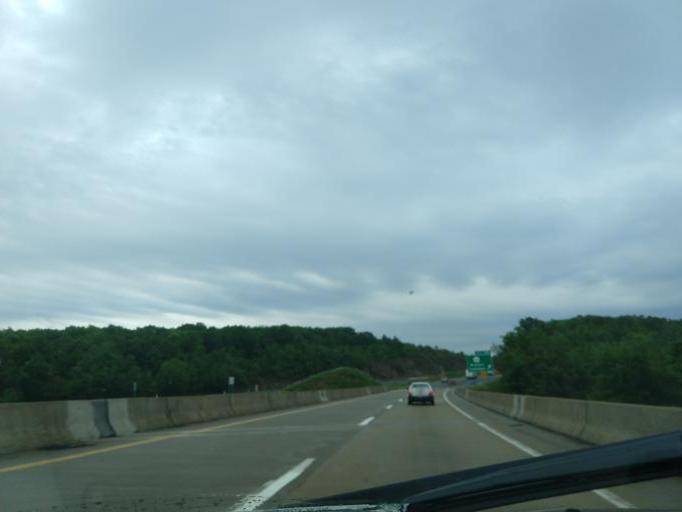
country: US
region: Pennsylvania
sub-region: Schuylkill County
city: McAdoo
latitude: 40.8759
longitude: -76.0225
